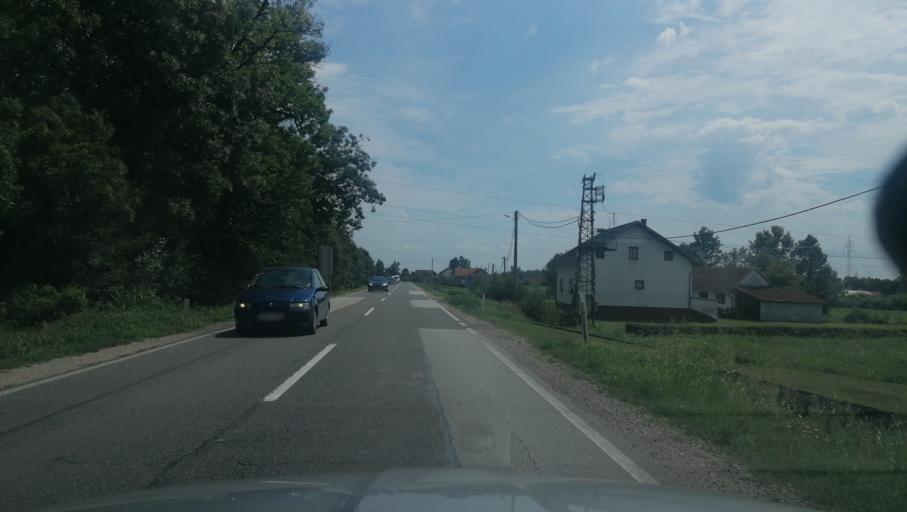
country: BA
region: Republika Srpska
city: Bosanski Samac
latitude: 45.0446
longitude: 18.4866
